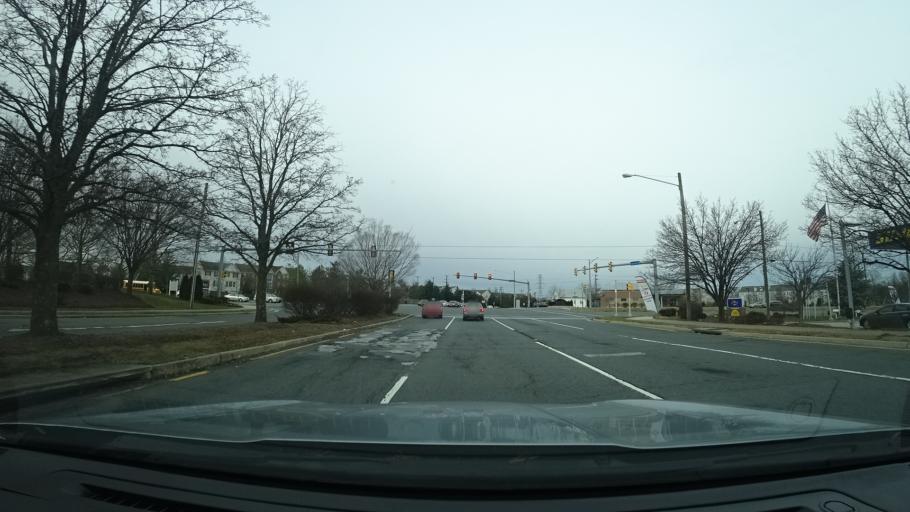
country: US
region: Virginia
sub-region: Fairfax County
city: Floris
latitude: 38.9479
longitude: -77.4124
